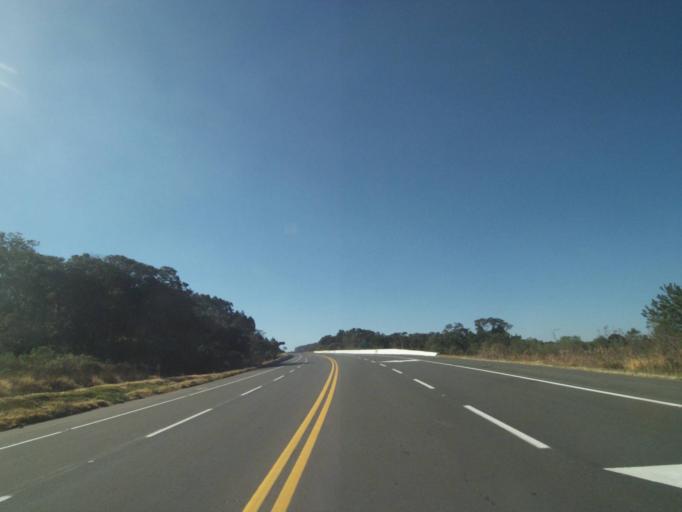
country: BR
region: Parana
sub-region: Tibagi
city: Tibagi
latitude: -24.8133
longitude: -50.4845
